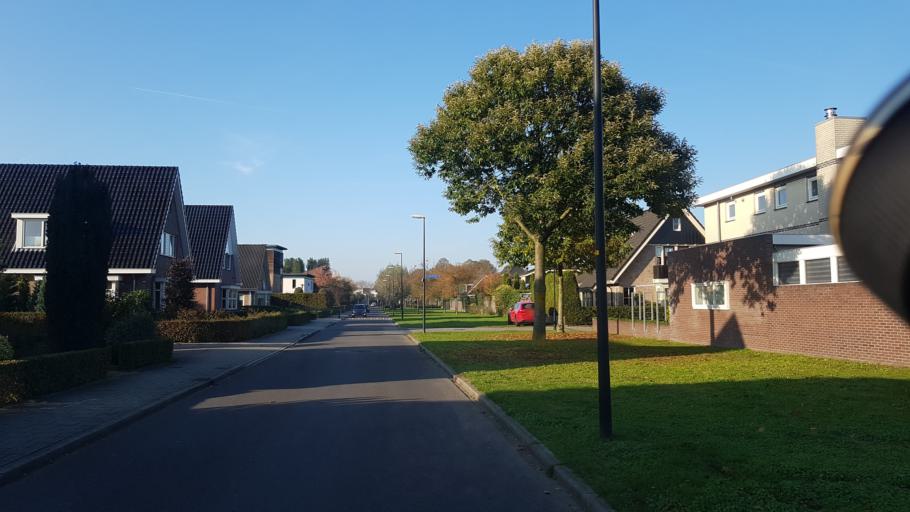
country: NL
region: Gelderland
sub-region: Gemeente Apeldoorn
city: Apeldoorn
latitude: 52.2147
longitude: 6.0184
